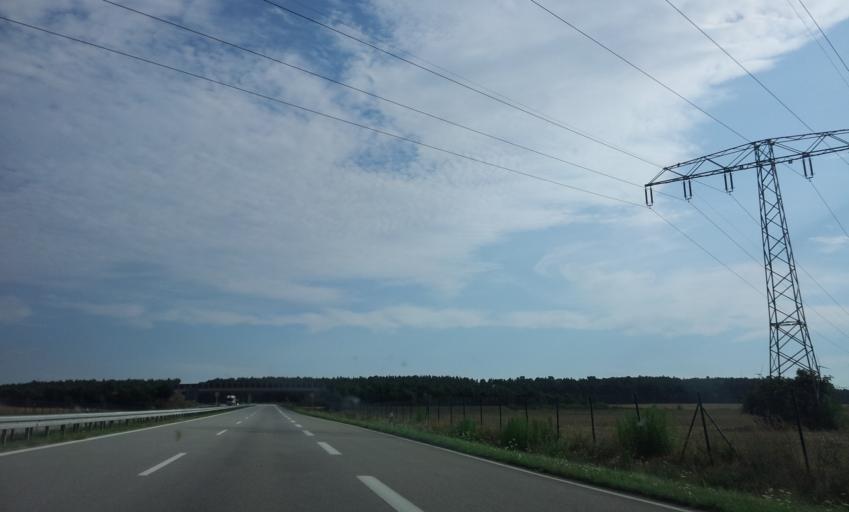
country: DE
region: Brandenburg
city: Trebbin
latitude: 52.1875
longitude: 13.2520
